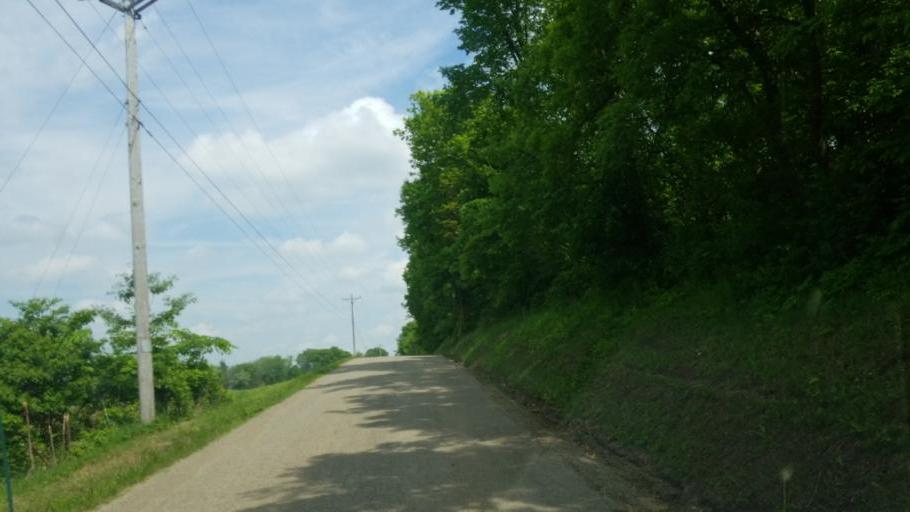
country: US
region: Ohio
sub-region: Ashland County
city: Loudonville
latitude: 40.6828
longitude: -82.3544
